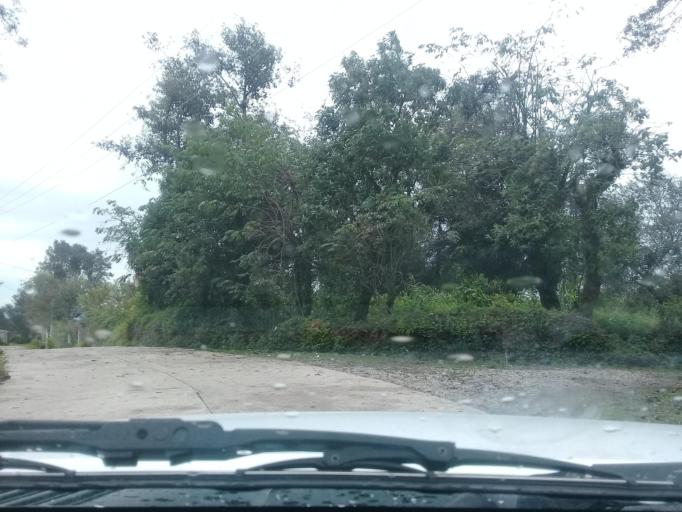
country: MX
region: Veracruz
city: Rafael Lucio
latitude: 19.6159
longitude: -96.9980
